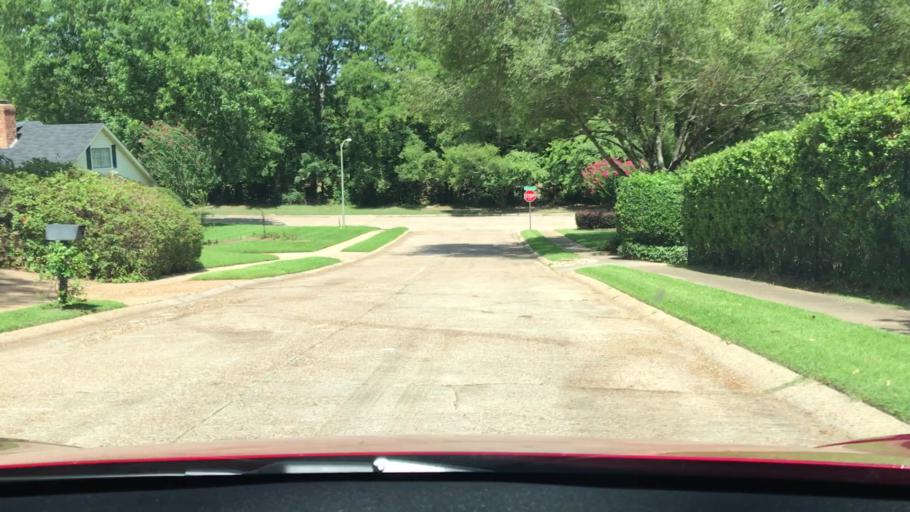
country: US
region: Louisiana
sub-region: Bossier Parish
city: Bossier City
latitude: 32.4299
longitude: -93.7288
